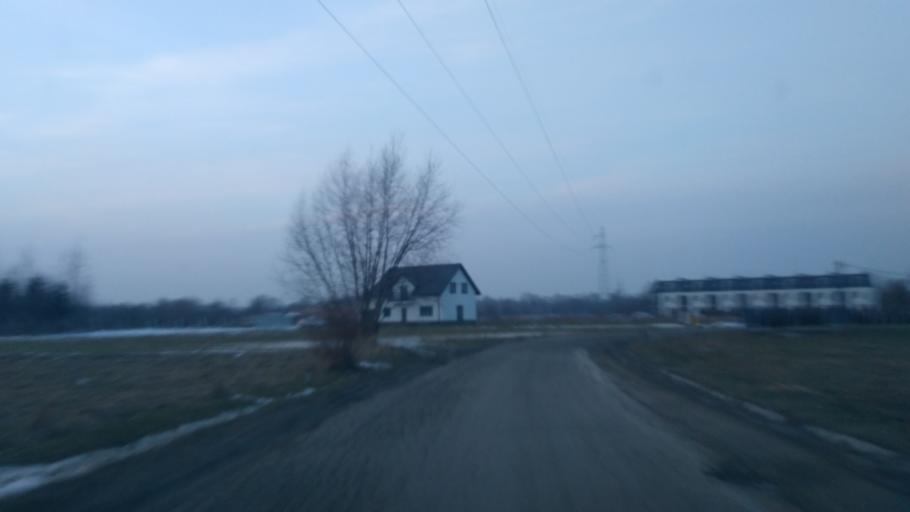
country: PL
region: Subcarpathian Voivodeship
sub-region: Powiat rzeszowski
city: Boguchwala
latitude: 49.9861
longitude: 21.9727
